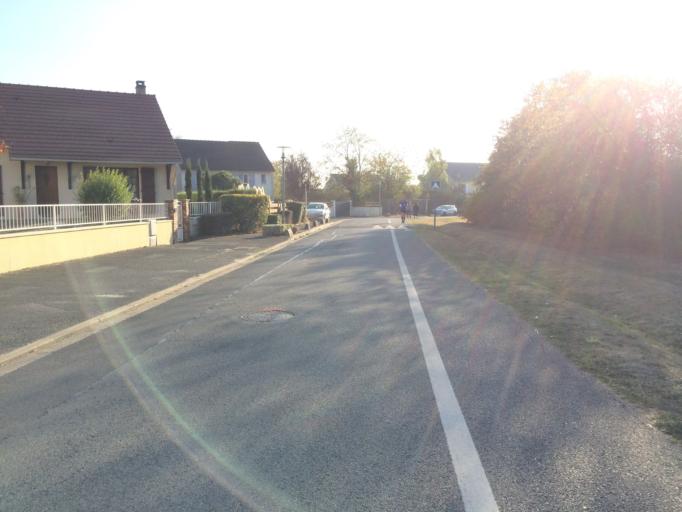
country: FR
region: Ile-de-France
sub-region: Departement de l'Essonne
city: Villejust
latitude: 48.6794
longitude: 2.2420
